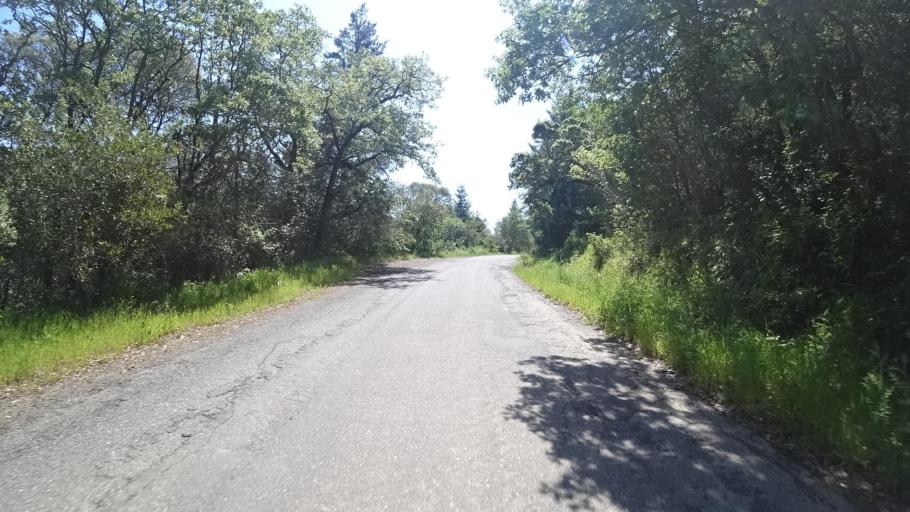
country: US
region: California
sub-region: Humboldt County
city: Redway
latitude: 40.1713
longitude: -123.6048
